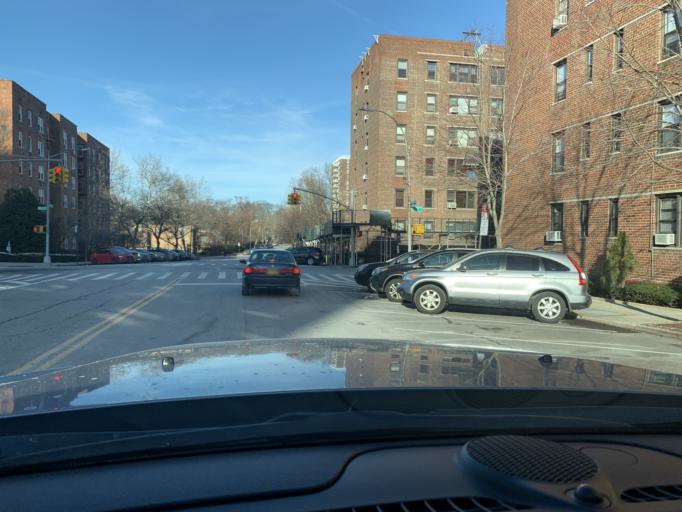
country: US
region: New York
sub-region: New York County
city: Inwood
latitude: 40.8894
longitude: -73.9130
